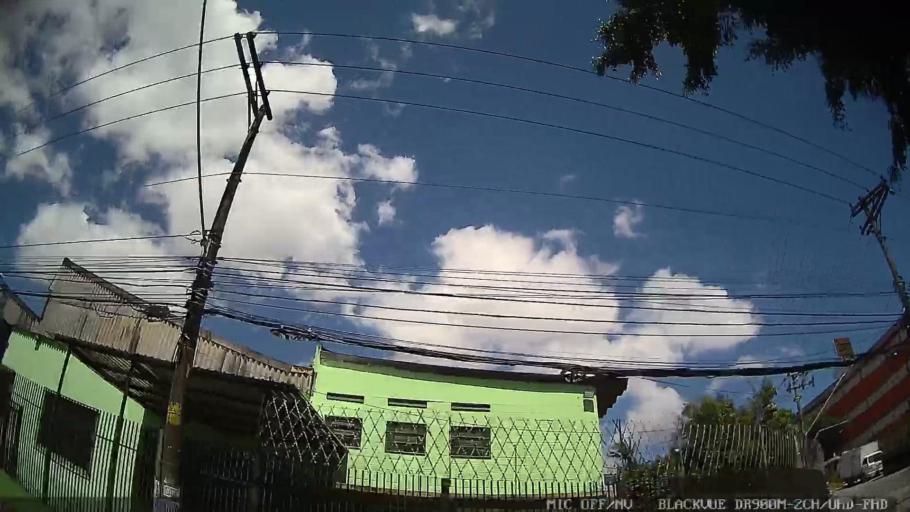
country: BR
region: Sao Paulo
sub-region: Diadema
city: Diadema
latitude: -23.6753
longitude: -46.6215
